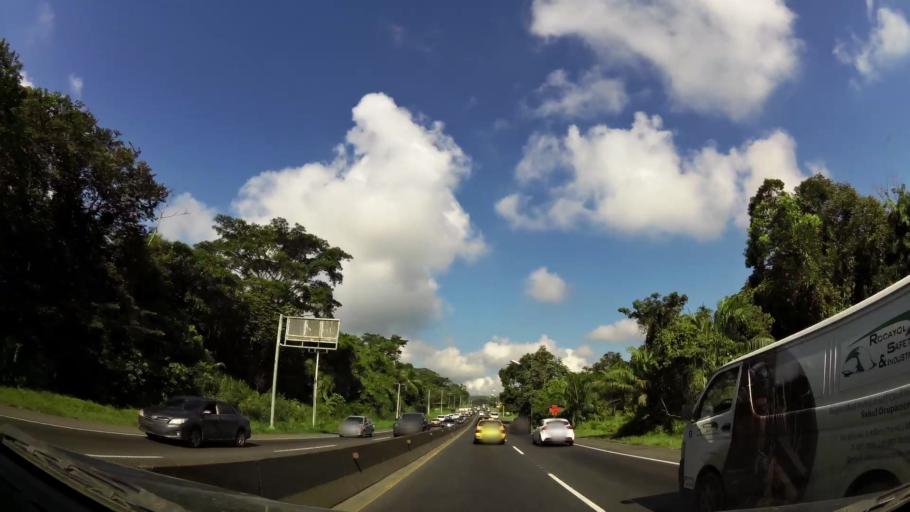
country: PA
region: Panama
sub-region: Distrito de Panama
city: Ancon
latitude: 8.9478
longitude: -79.5831
